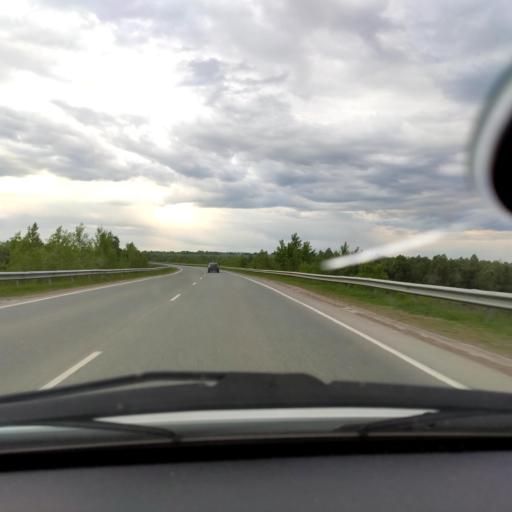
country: RU
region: Bashkortostan
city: Dyurtyuli
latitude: 55.5248
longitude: 54.8420
